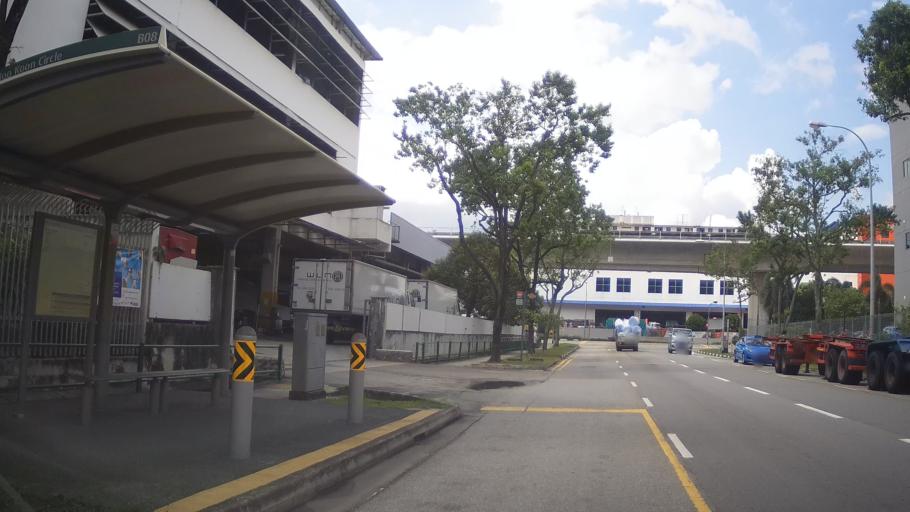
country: MY
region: Johor
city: Johor Bahru
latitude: 1.3268
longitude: 103.6767
